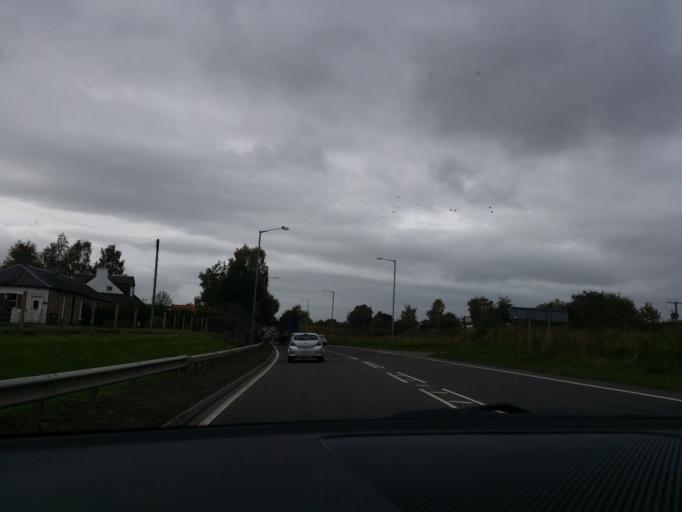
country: GB
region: Scotland
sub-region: Clackmannanshire
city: Clackmannan
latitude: 56.1135
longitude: -3.7503
